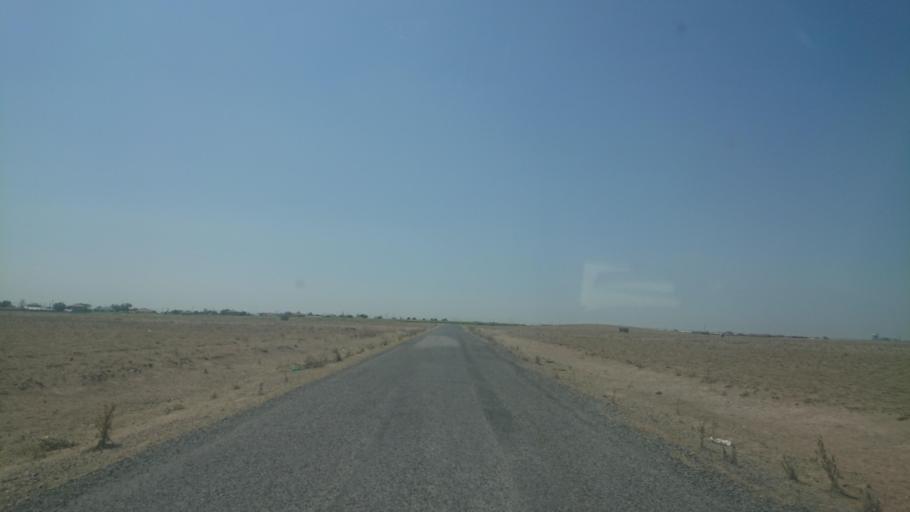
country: TR
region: Aksaray
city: Yesilova
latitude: 38.3004
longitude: 33.7309
